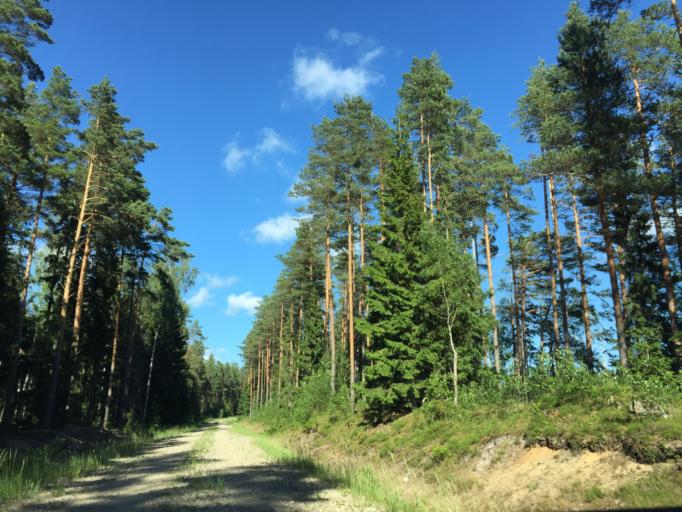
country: LV
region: Ventspils
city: Ventspils
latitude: 57.5433
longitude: 21.7614
